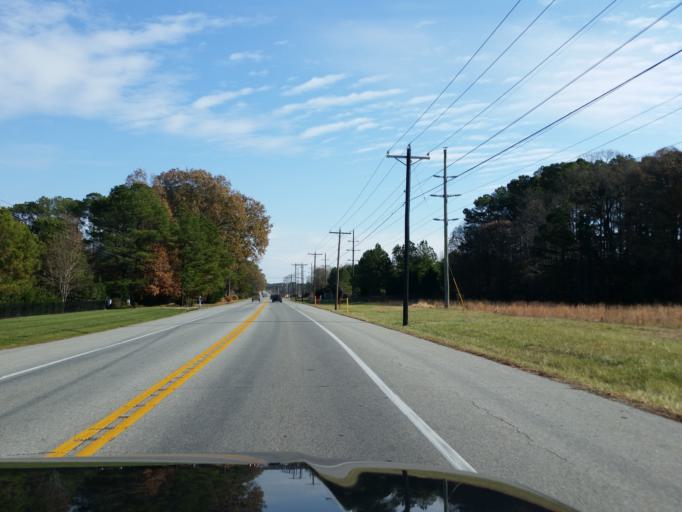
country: US
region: Maryland
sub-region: Talbot County
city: Saint Michaels
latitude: 38.7547
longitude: -76.1832
